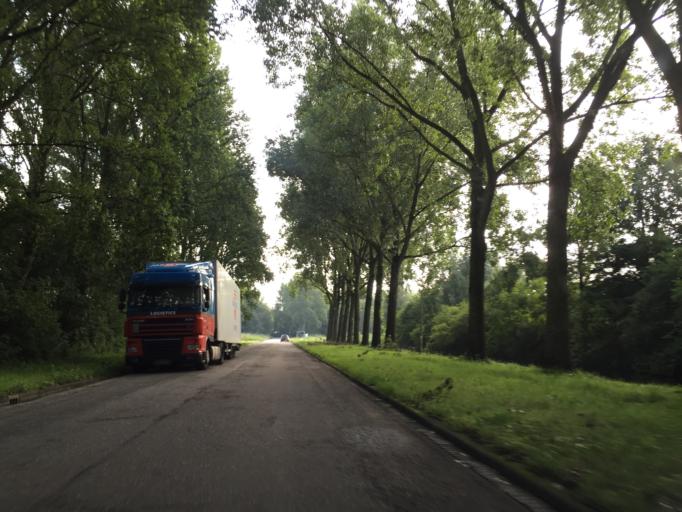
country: NL
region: South Holland
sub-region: Gemeente Rotterdam
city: Rotterdam
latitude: 51.9520
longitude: 4.4536
